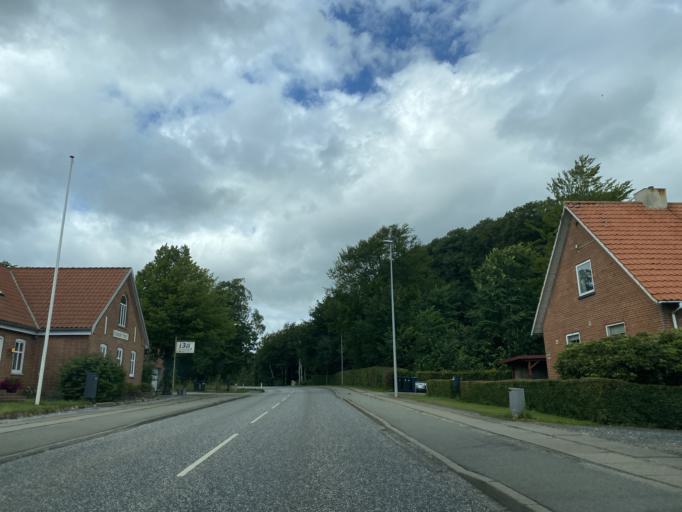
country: DK
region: Central Jutland
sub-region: Silkeborg Kommune
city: Svejbaek
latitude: 56.2278
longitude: 9.6298
